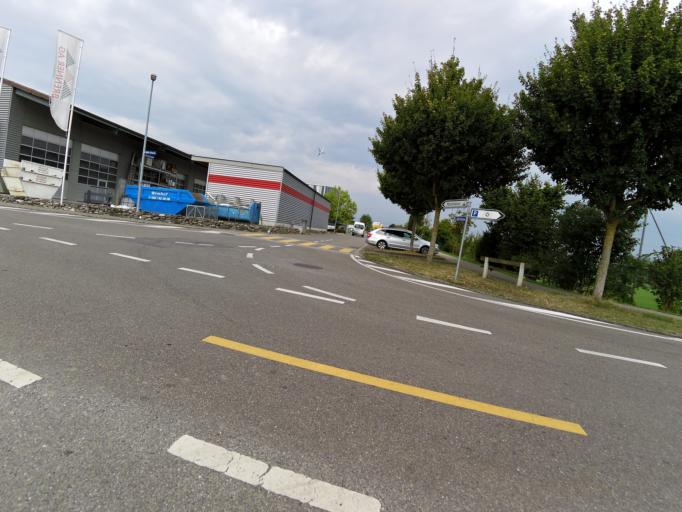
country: CH
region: Thurgau
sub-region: Kreuzlingen District
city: Tagerwilen
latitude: 47.6554
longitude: 9.1444
